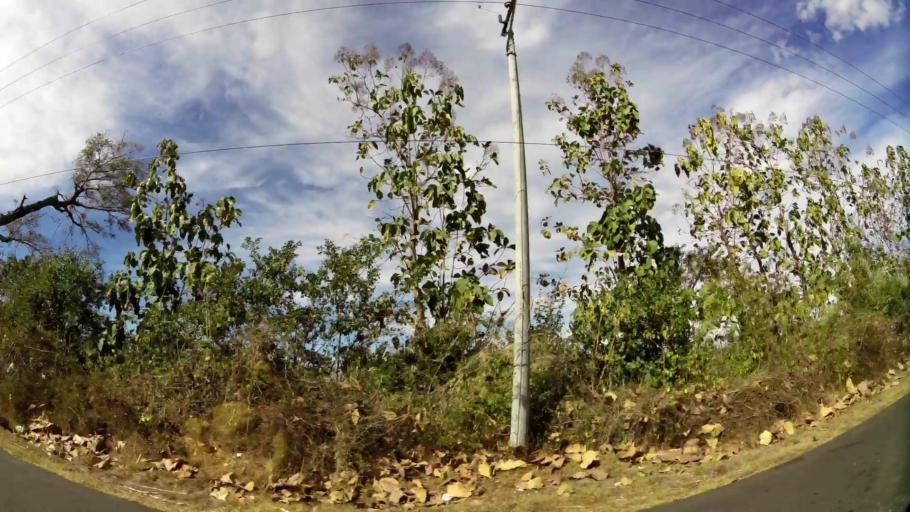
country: SV
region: San Salvador
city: Aguilares
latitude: 13.9616
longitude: -89.1294
